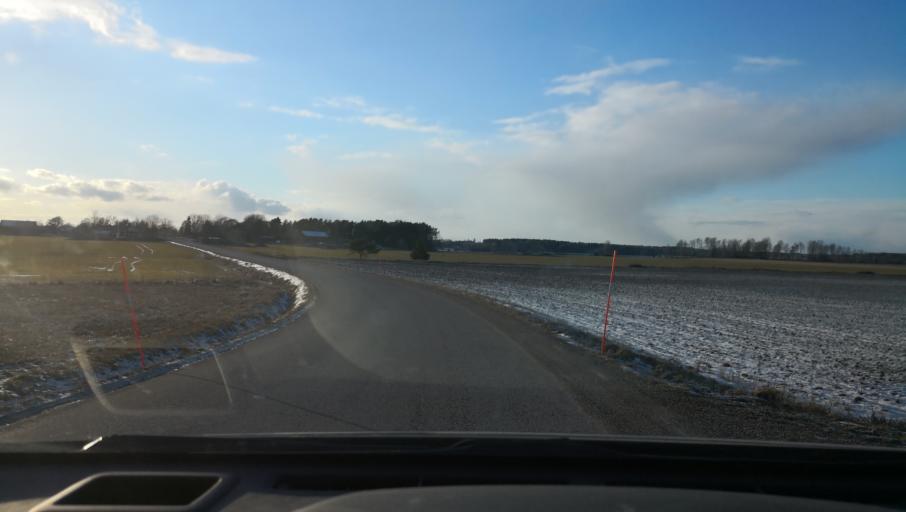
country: SE
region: Vaestmanland
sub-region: Vasteras
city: Tillberga
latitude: 59.6393
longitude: 16.7145
